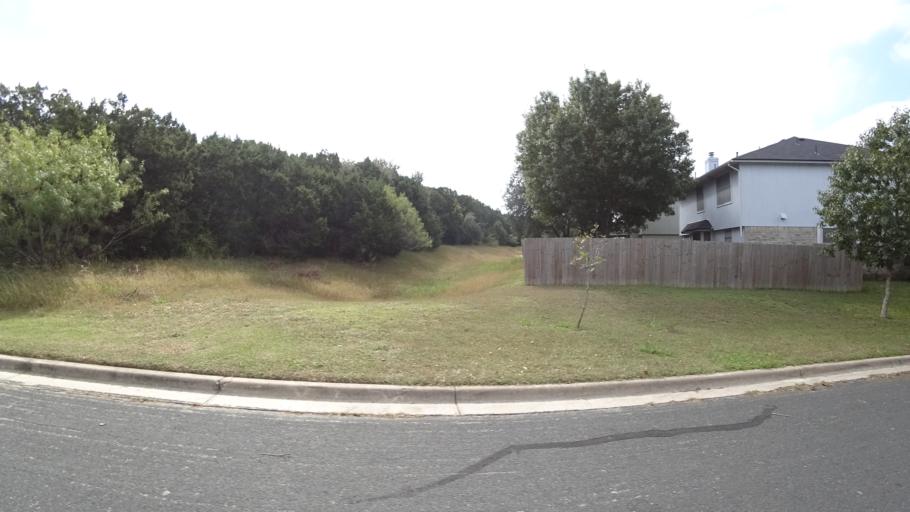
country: US
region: Texas
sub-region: Travis County
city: Shady Hollow
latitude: 30.1940
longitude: -97.8331
